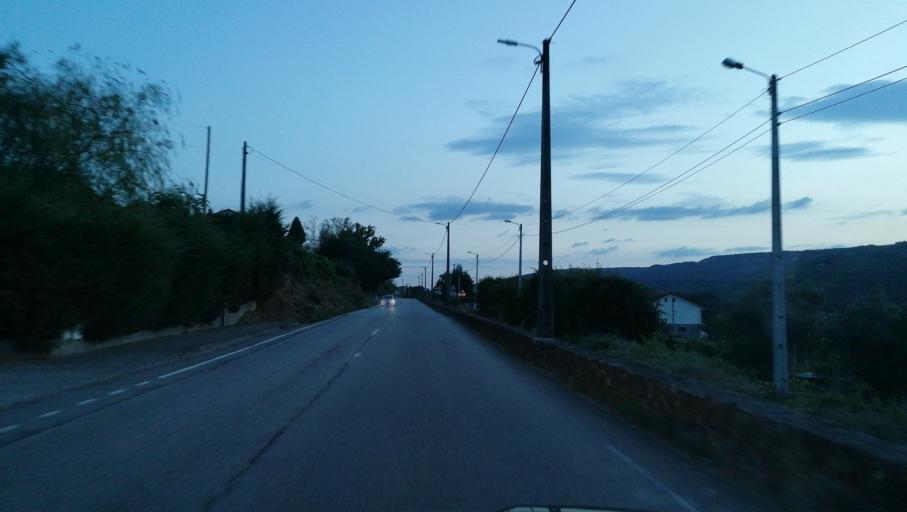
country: PT
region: Vila Real
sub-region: Vila Pouca de Aguiar
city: Vila Pouca de Aguiar
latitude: 41.5393
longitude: -7.6055
